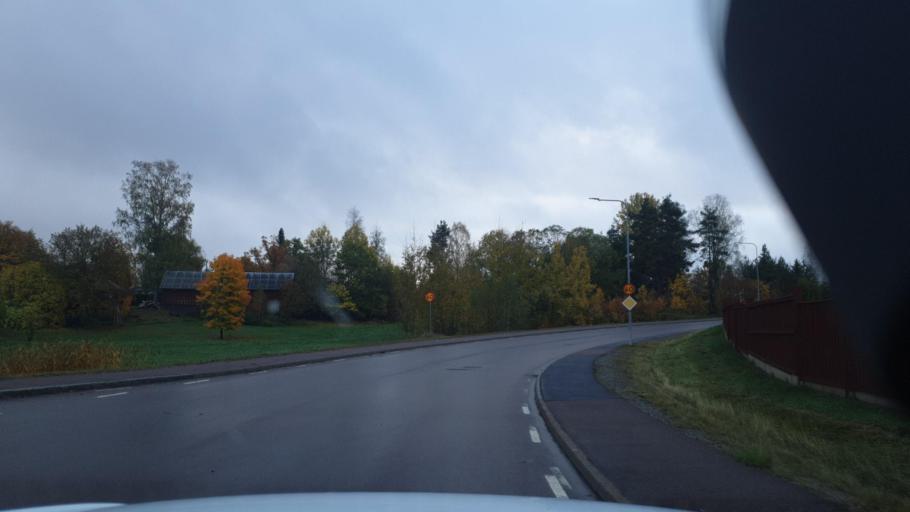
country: SE
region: Vaermland
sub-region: Arvika Kommun
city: Arvika
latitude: 59.6304
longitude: 12.8178
